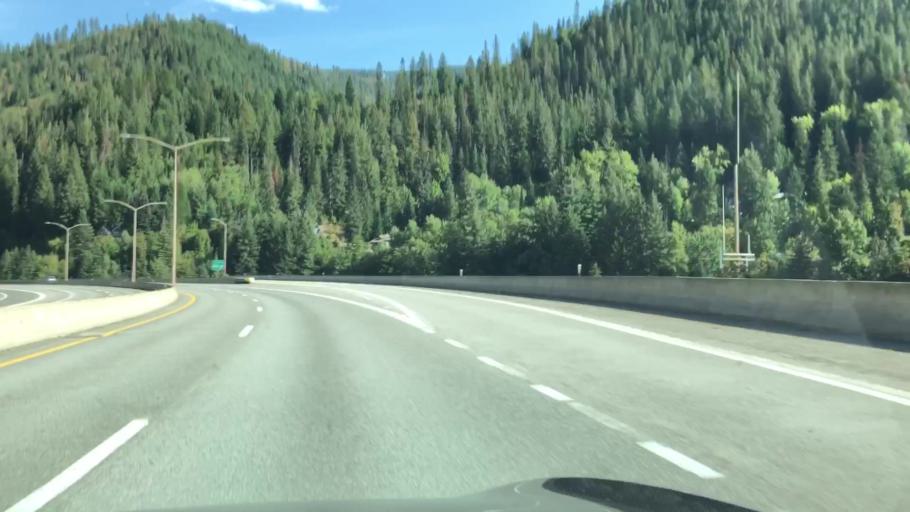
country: US
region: Idaho
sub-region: Shoshone County
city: Wallace
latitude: 47.4725
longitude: -115.9215
